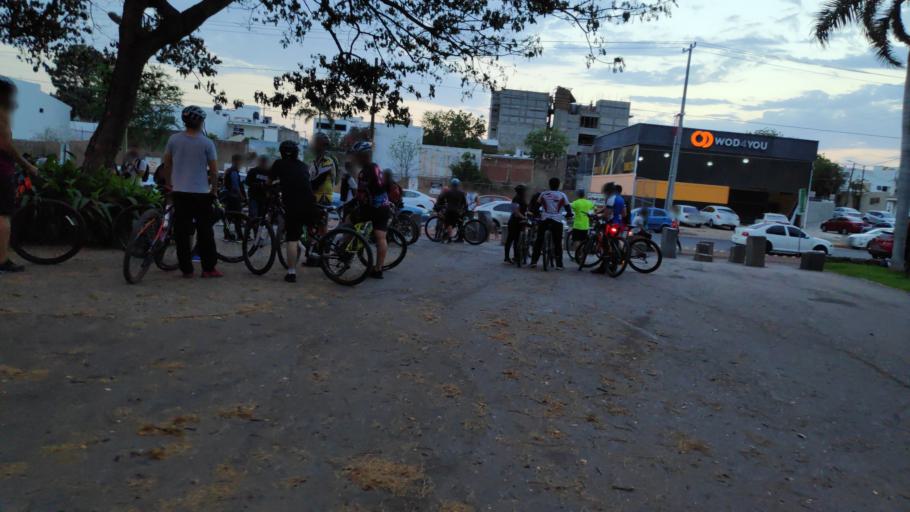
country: MX
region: Sinaloa
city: Culiacan
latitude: 24.8238
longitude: -107.3876
